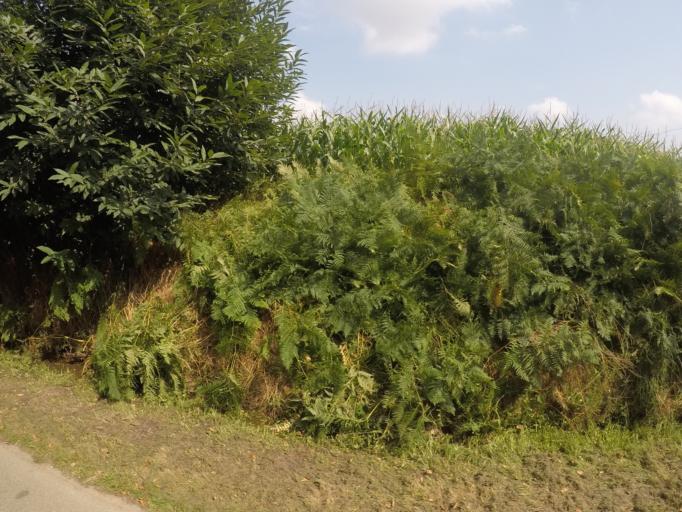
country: FR
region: Brittany
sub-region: Departement des Cotes-d'Armor
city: Saint-Donan
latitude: 48.5000
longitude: -2.9130
